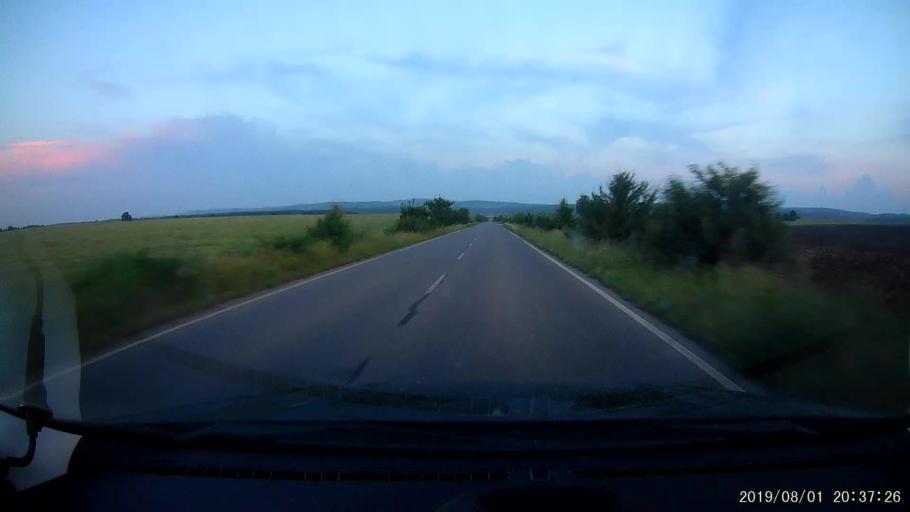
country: BG
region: Yambol
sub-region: Obshtina Elkhovo
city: Elkhovo
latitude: 42.0484
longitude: 26.5942
